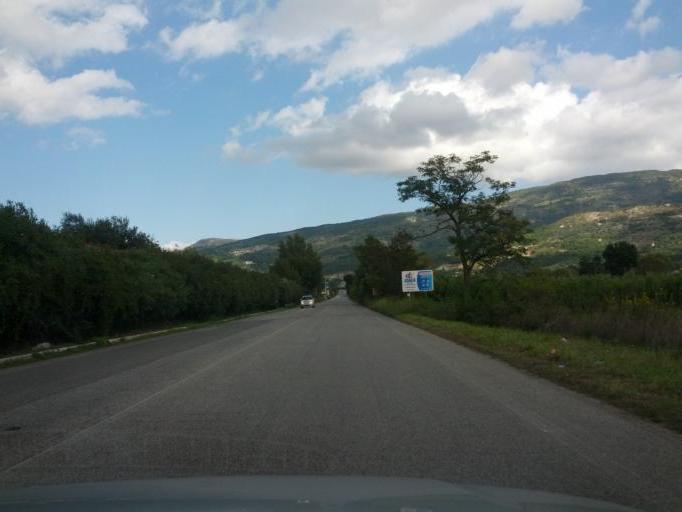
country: IT
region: Latium
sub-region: Provincia di Latina
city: Spigno Saturnia Inferiore
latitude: 41.3243
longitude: 13.7451
